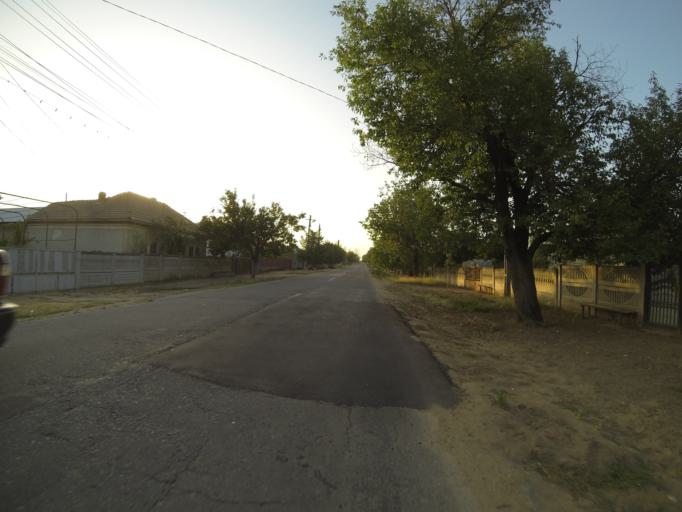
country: RO
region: Dolj
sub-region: Comuna Daneti
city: Daneti
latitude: 43.9794
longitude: 24.0295
